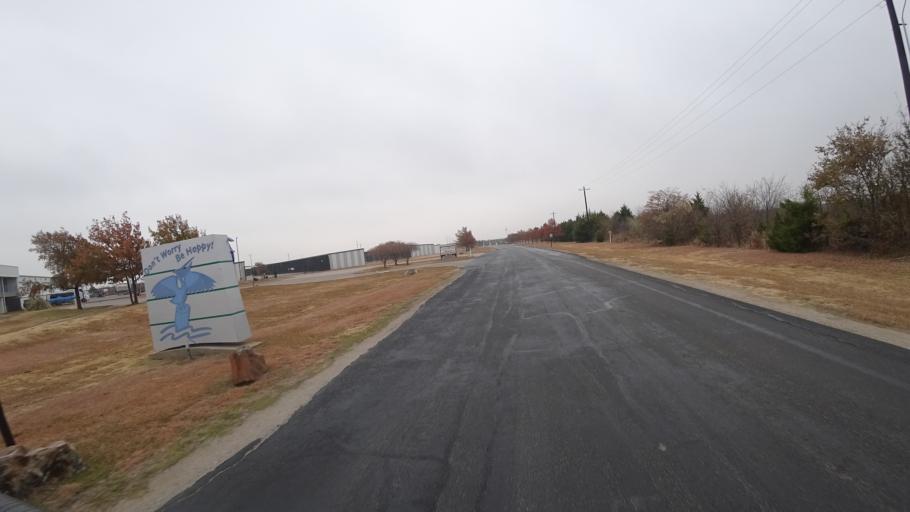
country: US
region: Texas
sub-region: Denton County
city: The Colony
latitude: 33.0718
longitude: -96.9205
